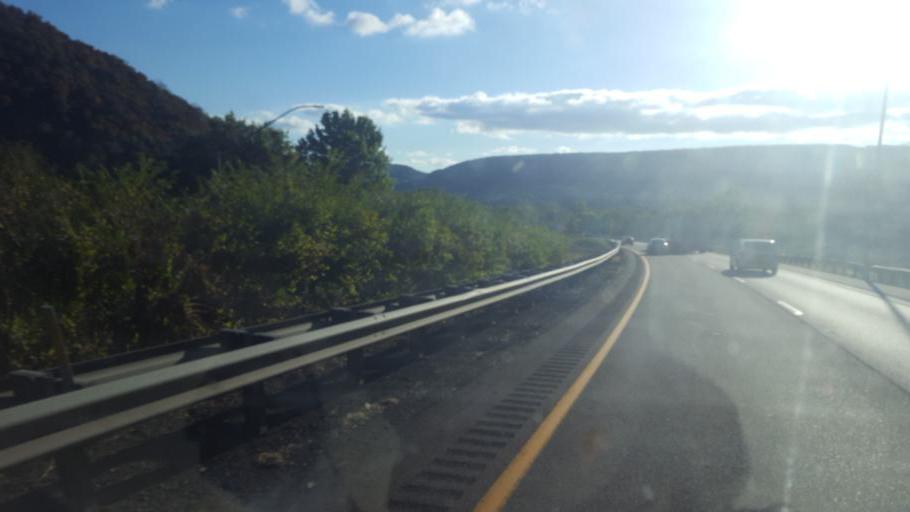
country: US
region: Maryland
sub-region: Allegany County
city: La Vale
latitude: 39.6350
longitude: -78.8450
